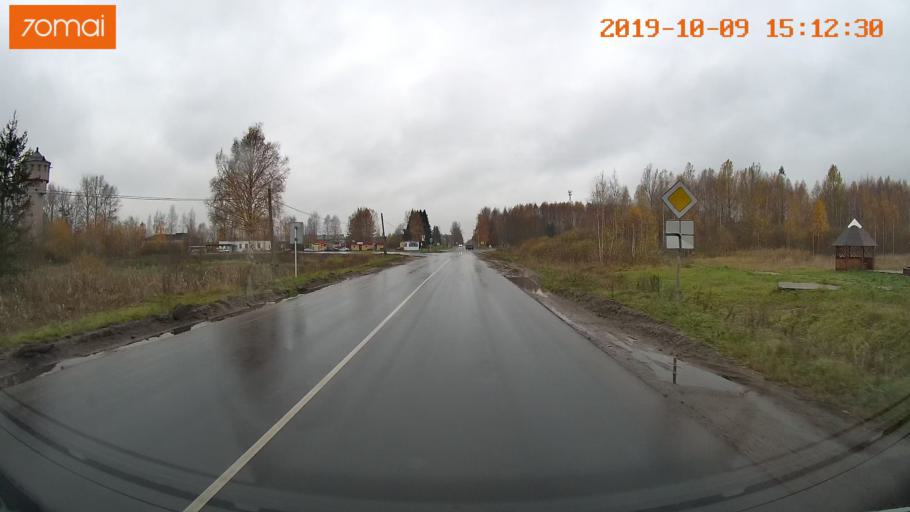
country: RU
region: Kostroma
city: Susanino
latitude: 58.1549
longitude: 41.6154
